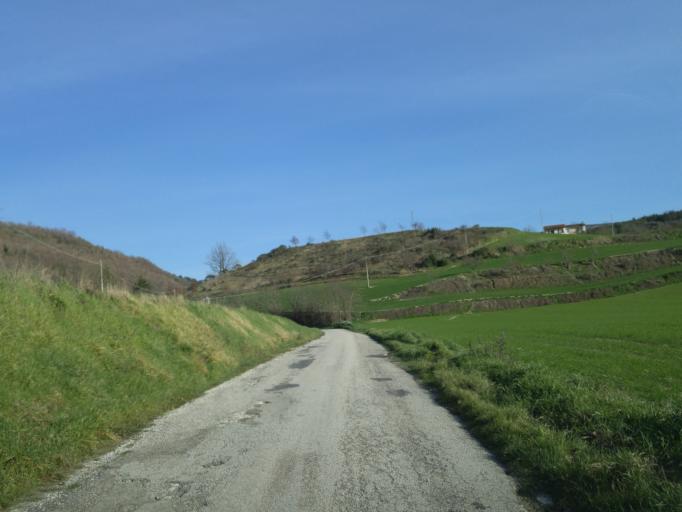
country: IT
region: The Marches
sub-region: Provincia di Pesaro e Urbino
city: Fermignano
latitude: 43.6784
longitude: 12.6621
